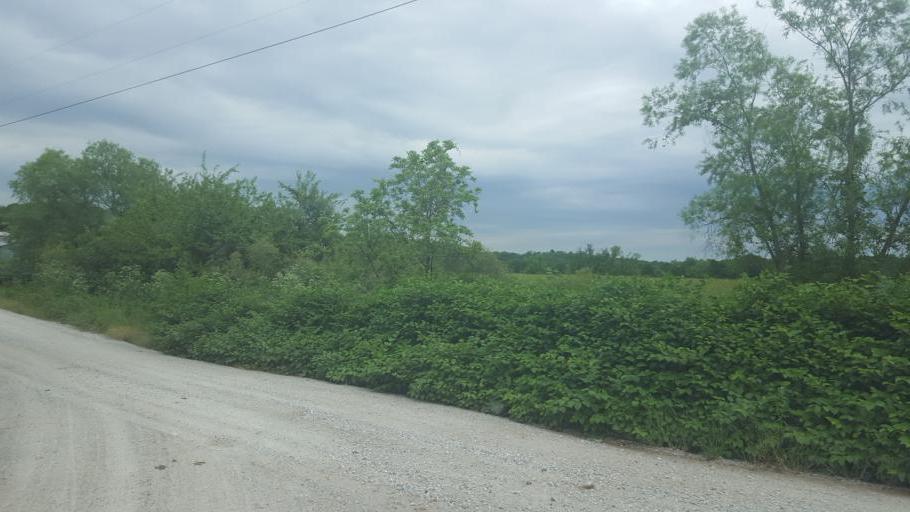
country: US
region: Missouri
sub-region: Moniteau County
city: California
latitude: 38.7366
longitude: -92.6093
